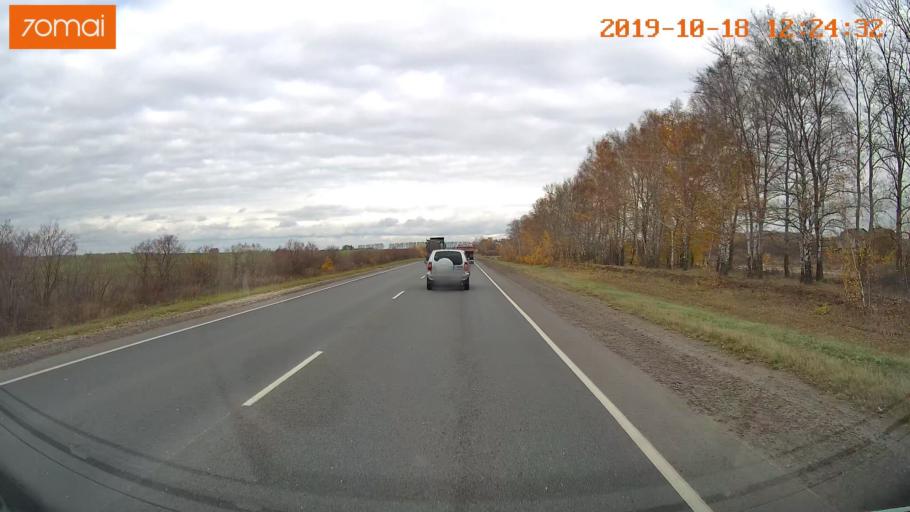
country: RU
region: Rjazan
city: Rybnoye
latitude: 54.5400
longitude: 39.5138
